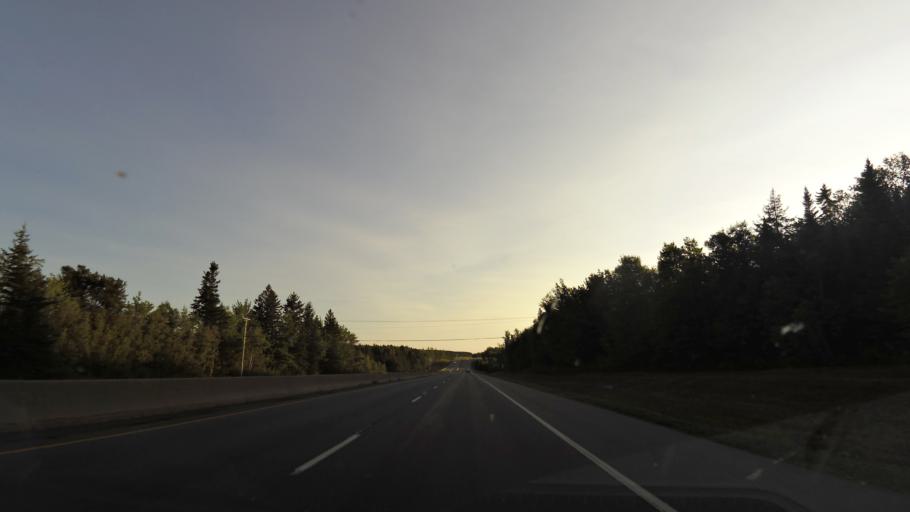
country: CA
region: New Brunswick
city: Salisbury
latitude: 45.9244
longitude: -65.1751
